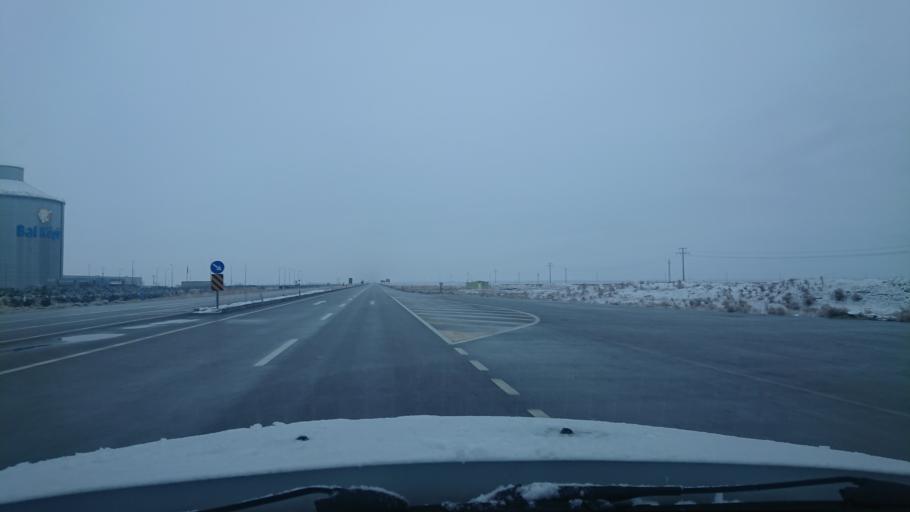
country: TR
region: Aksaray
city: Sultanhani
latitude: 38.2688
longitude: 33.6636
